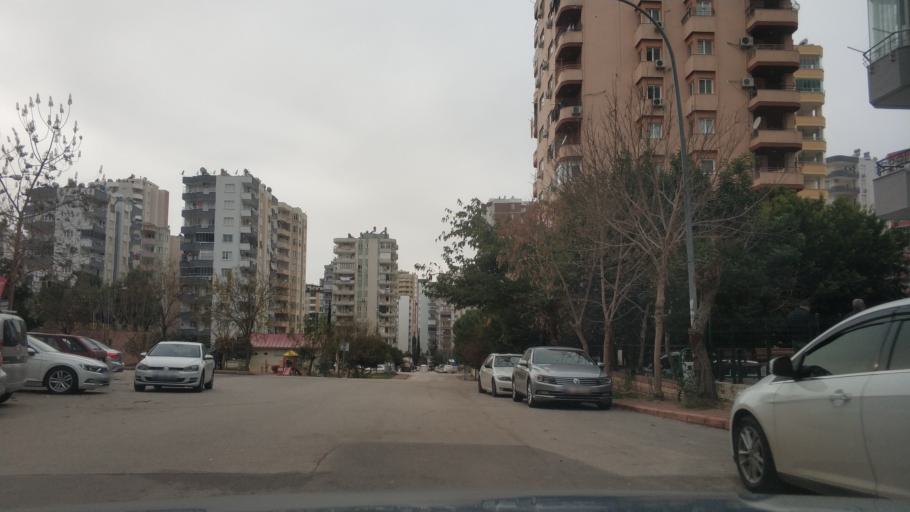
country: TR
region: Adana
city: Adana
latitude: 37.0553
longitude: 35.2807
